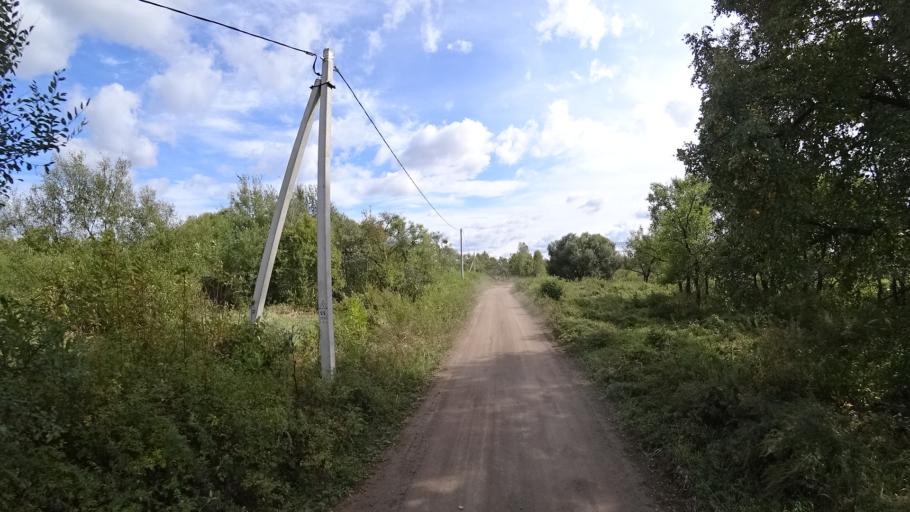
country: RU
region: Amur
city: Arkhara
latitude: 49.3486
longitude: 130.1615
